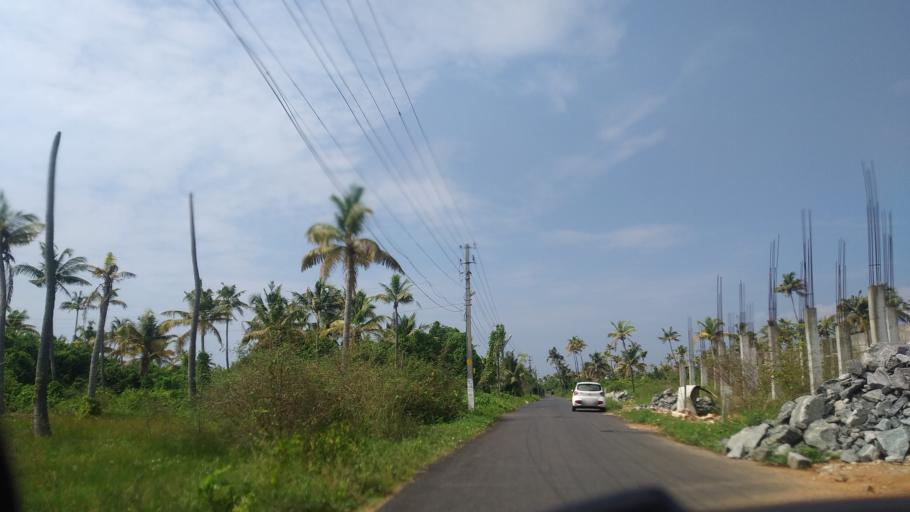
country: IN
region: Kerala
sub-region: Ernakulam
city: Elur
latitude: 10.0448
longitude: 76.2087
